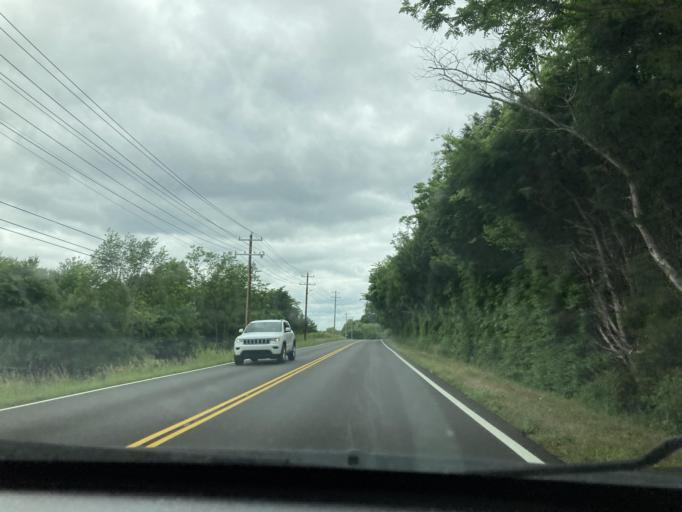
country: US
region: Tennessee
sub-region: Dickson County
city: Burns
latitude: 36.0540
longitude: -87.3470
